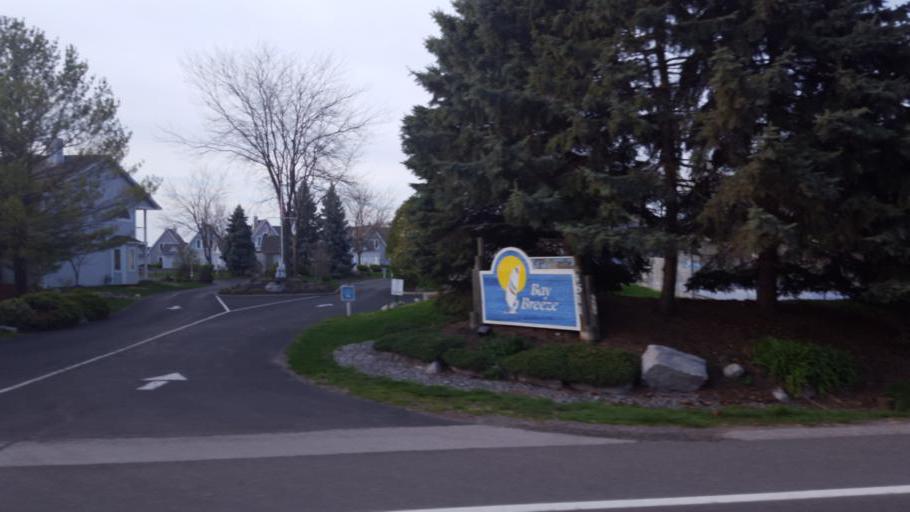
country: US
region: Ohio
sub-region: Erie County
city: Huron
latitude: 41.3826
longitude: -82.4680
